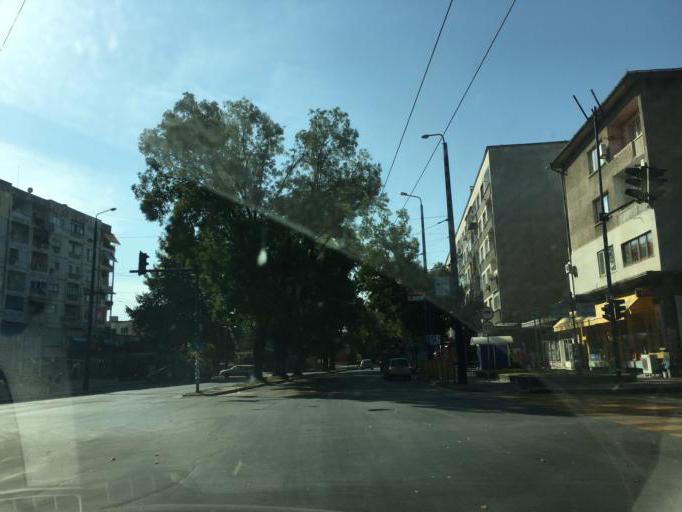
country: BG
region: Pazardzhik
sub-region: Obshtina Pazardzhik
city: Pazardzhik
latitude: 42.1995
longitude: 24.3330
